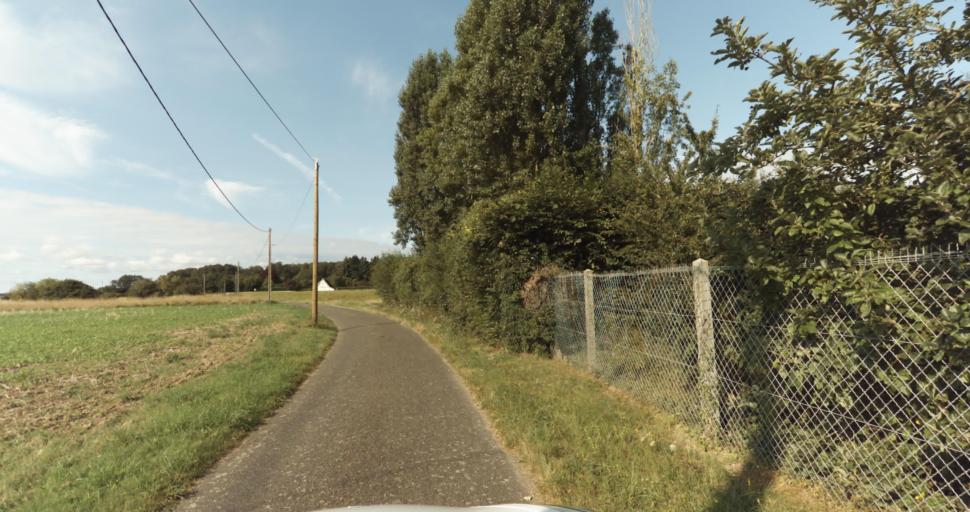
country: FR
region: Haute-Normandie
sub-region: Departement de l'Eure
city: Tillieres-sur-Avre
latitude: 48.8003
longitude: 1.1147
